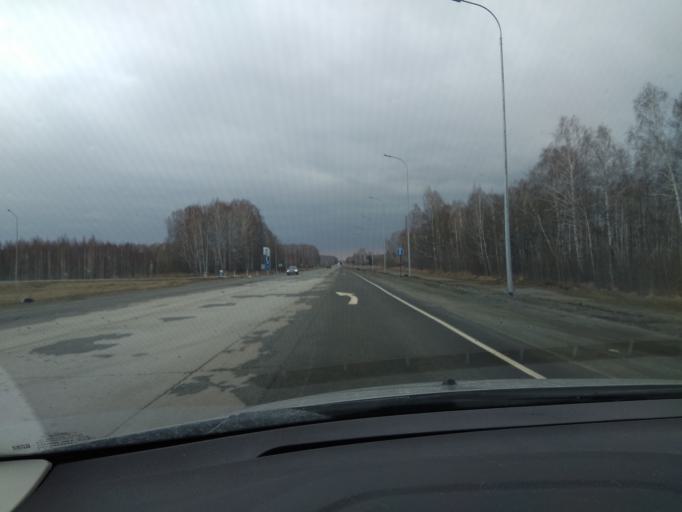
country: RU
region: Chelyabinsk
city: Tyubuk
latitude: 55.9845
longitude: 61.0214
